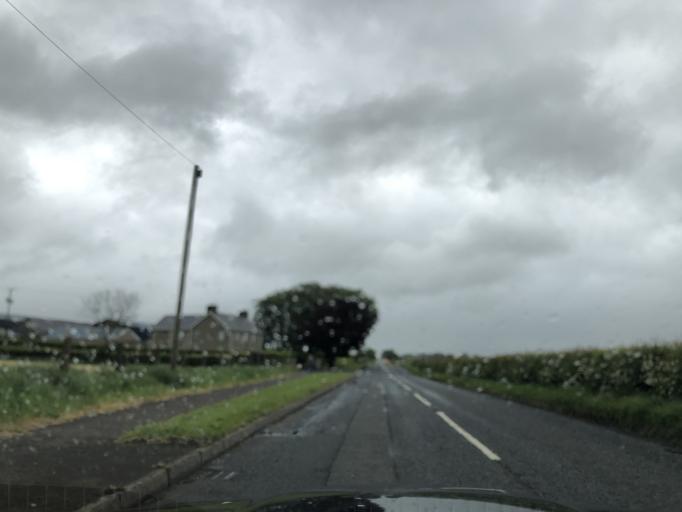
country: GB
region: Northern Ireland
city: Bushmills
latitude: 55.1491
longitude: -6.4423
